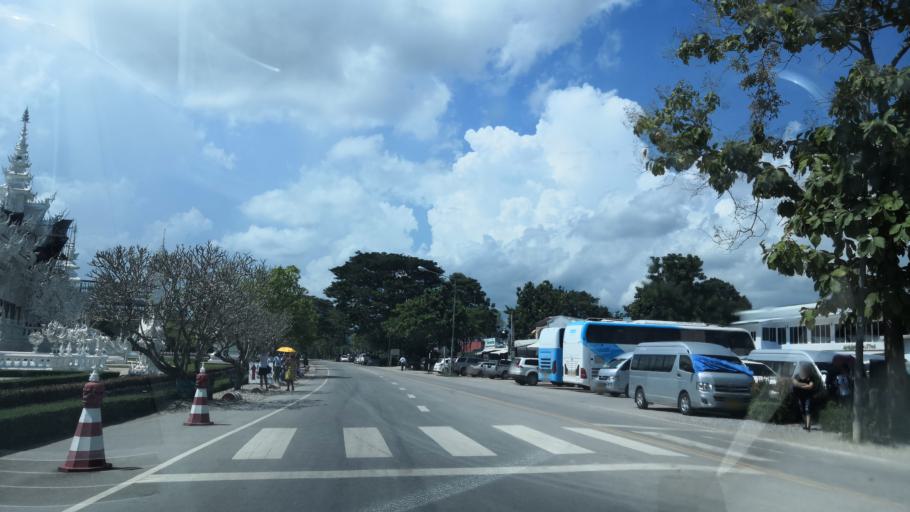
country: TH
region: Chiang Rai
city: Mae Lao
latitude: 19.8243
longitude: 99.7640
